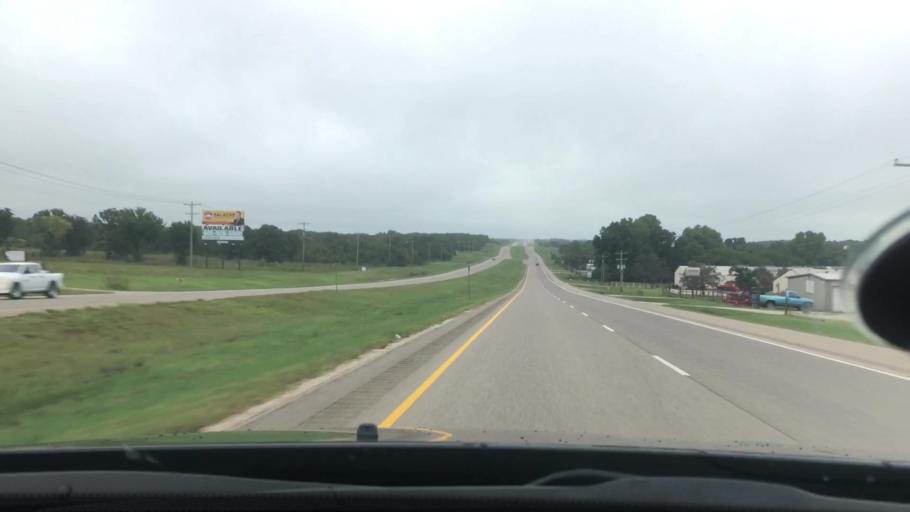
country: US
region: Oklahoma
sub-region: Seminole County
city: Seminole
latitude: 35.3196
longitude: -96.6713
